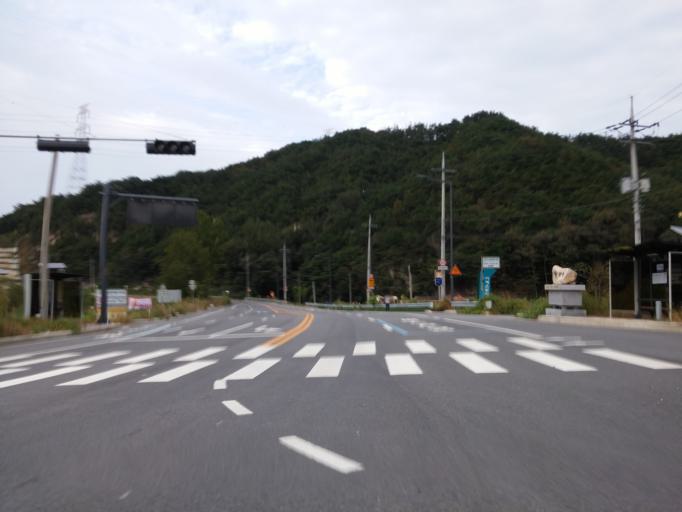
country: KR
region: Daejeon
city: Daejeon
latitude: 36.2317
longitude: 127.3162
